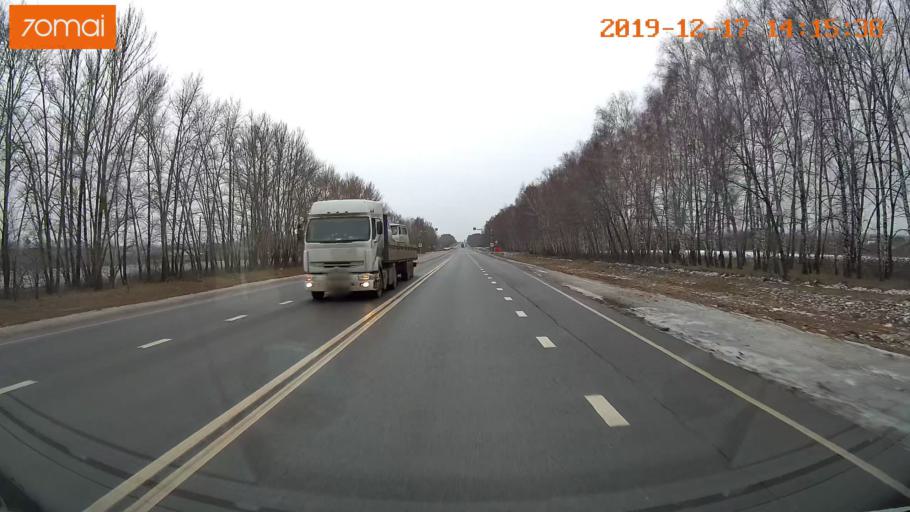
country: RU
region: Rjazan
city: Zakharovo
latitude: 54.4887
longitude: 39.4730
